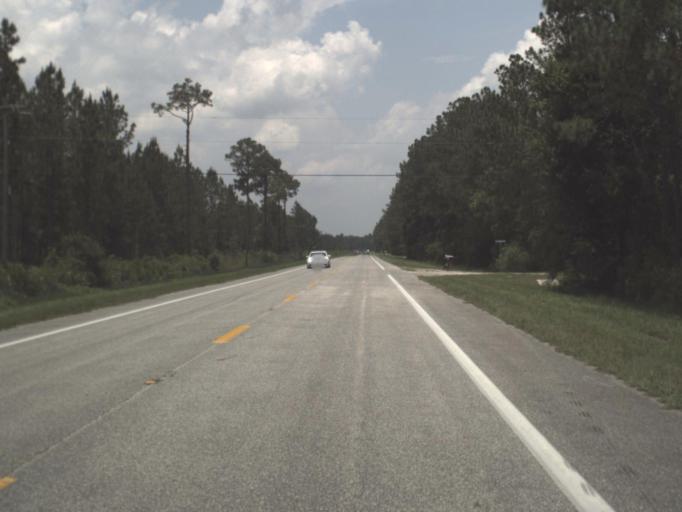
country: US
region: Florida
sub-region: Putnam County
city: Palatka
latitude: 29.5820
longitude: -81.7175
